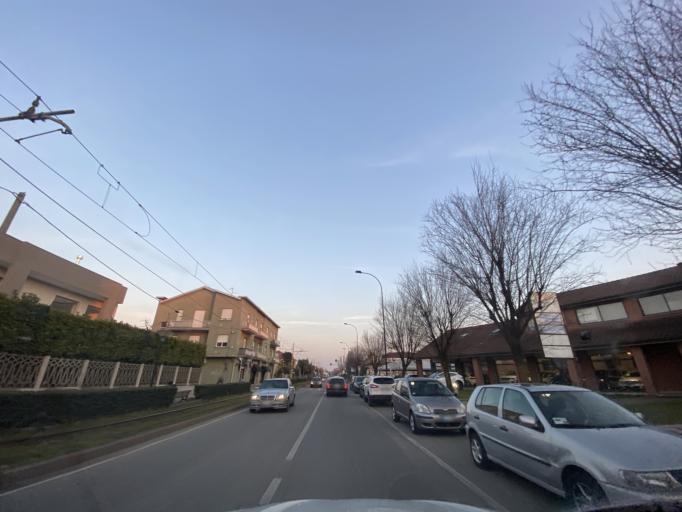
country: IT
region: Lombardy
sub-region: Provincia di Monza e Brianza
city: Limbiate
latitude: 45.6009
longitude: 9.1279
